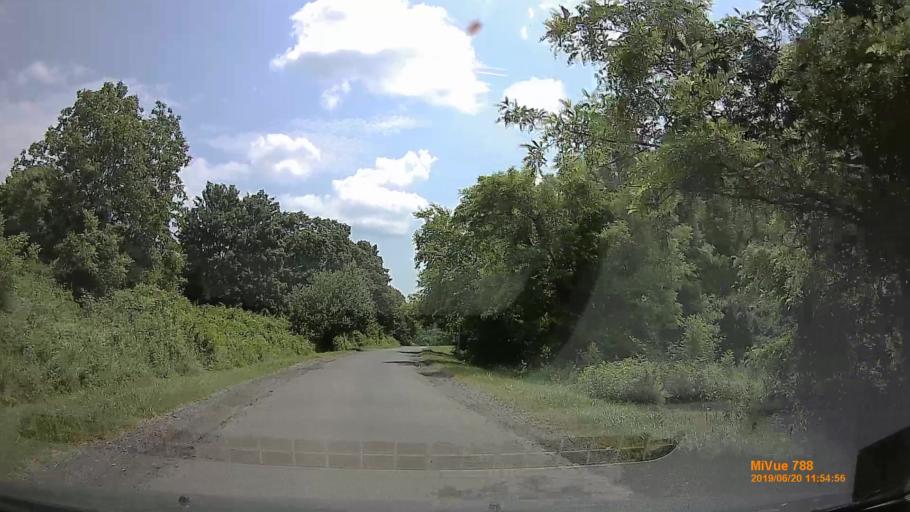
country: HU
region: Baranya
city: Mecseknadasd
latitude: 46.2250
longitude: 18.4440
